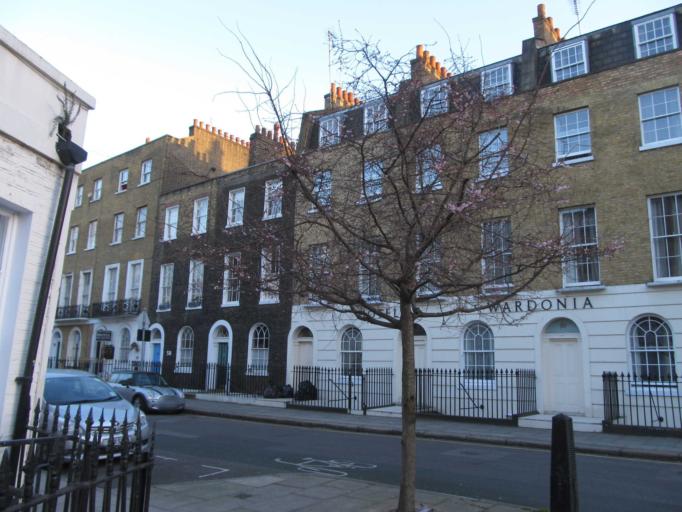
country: GB
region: England
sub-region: Greater London
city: Clerkenwell
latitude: 51.5286
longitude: -0.1231
